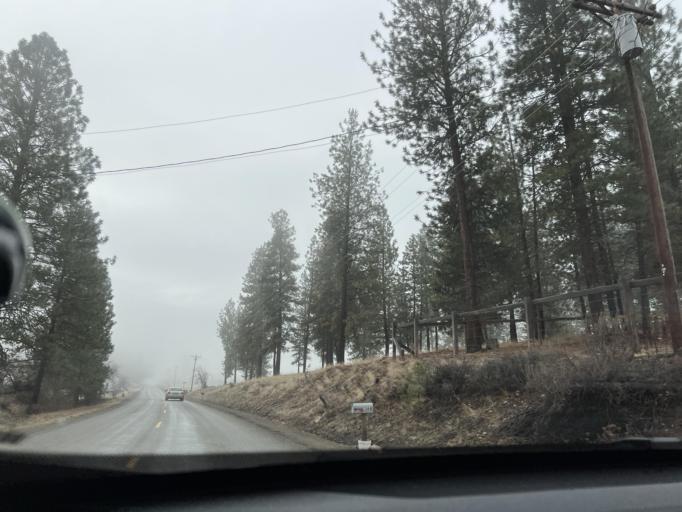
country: US
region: Washington
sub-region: Okanogan County
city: Brewster
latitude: 48.4630
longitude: -120.2074
